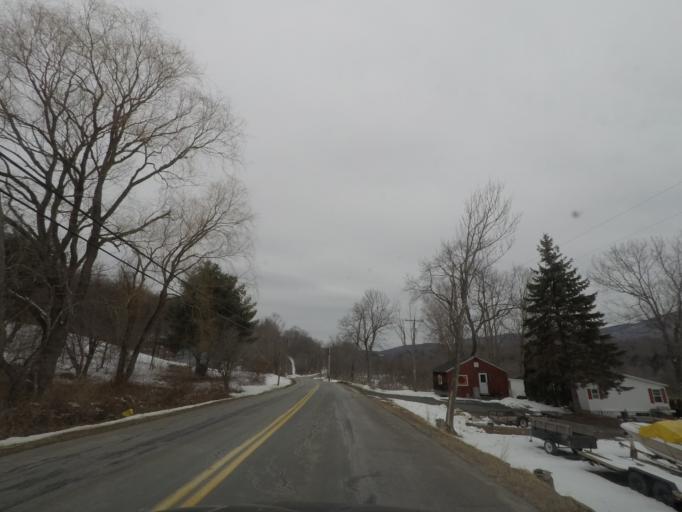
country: US
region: Massachusetts
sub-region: Berkshire County
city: Lanesborough
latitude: 42.5794
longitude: -73.3759
